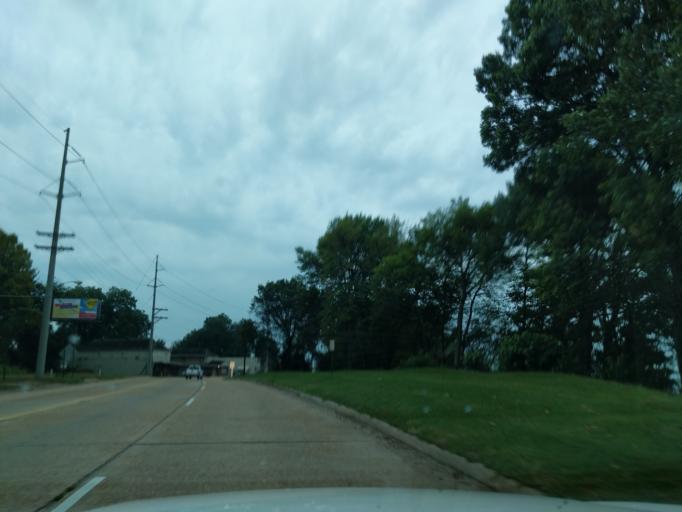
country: US
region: Mississippi
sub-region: Warren County
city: Vicksburg
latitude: 32.3217
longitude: -90.8963
